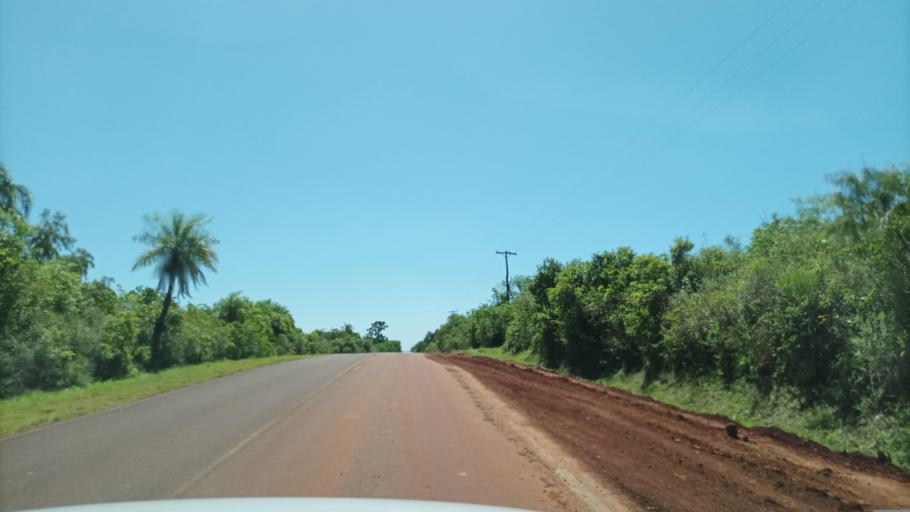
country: AR
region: Misiones
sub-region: Departamento de Apostoles
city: San Jose
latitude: -27.7733
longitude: -55.7526
